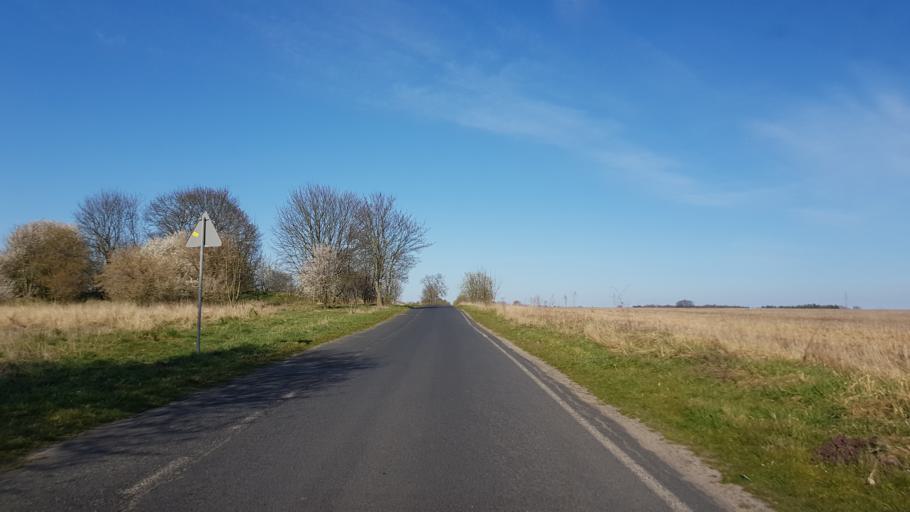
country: PL
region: West Pomeranian Voivodeship
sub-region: Powiat stargardzki
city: Stargard Szczecinski
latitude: 53.4053
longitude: 15.0324
